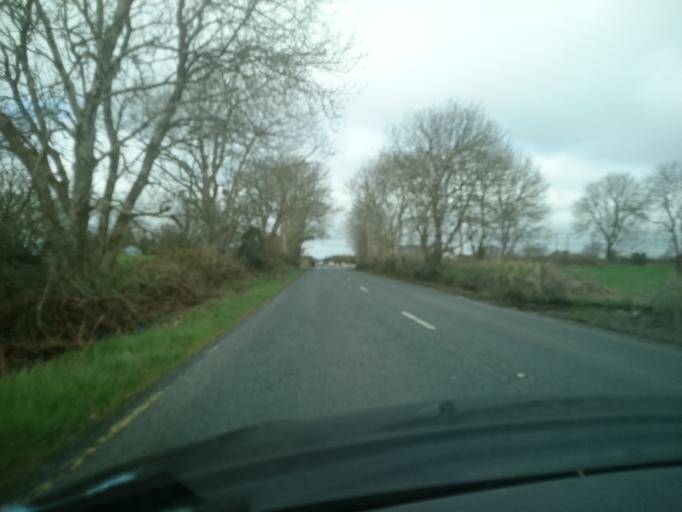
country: IE
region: Connaught
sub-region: Maigh Eo
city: Claremorris
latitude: 53.7493
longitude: -9.0262
